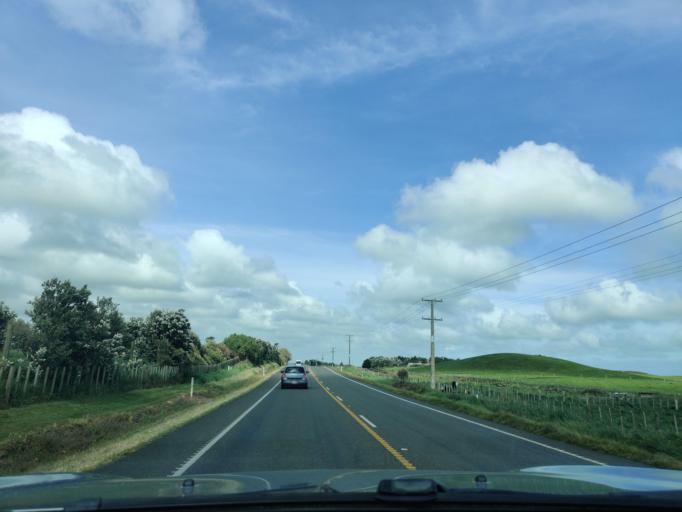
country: NZ
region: Taranaki
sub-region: South Taranaki District
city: Patea
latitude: -39.7723
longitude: 174.6722
